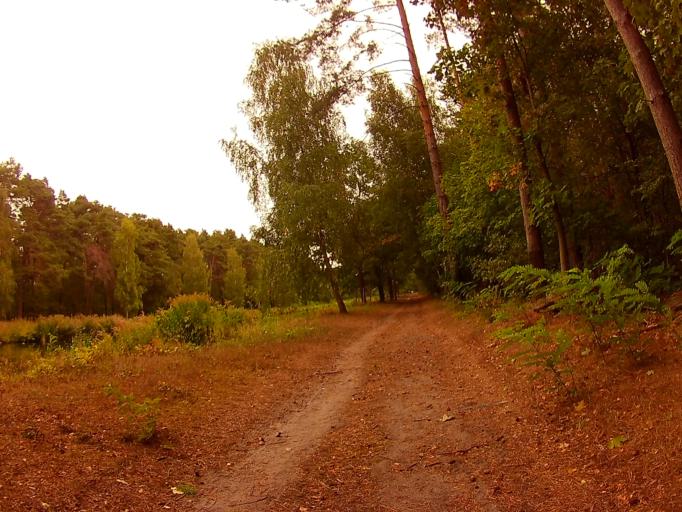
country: DE
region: Berlin
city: Schmockwitz
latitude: 52.3764
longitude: 13.6850
